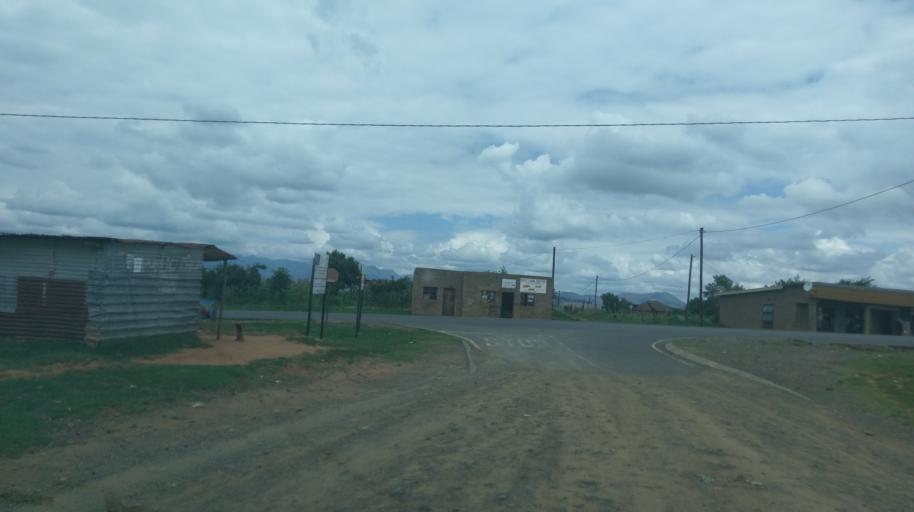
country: LS
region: Leribe
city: Leribe
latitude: -28.9357
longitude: 28.1535
